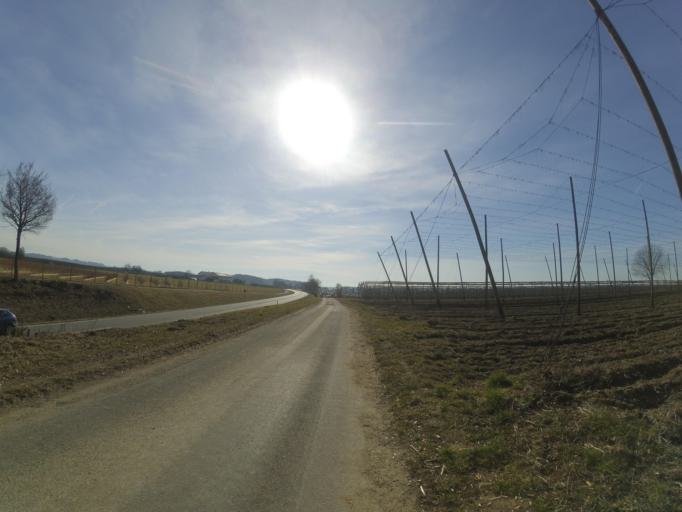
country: DE
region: Baden-Wuerttemberg
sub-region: Tuebingen Region
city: Meckenbeuren
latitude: 47.7241
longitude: 9.5849
